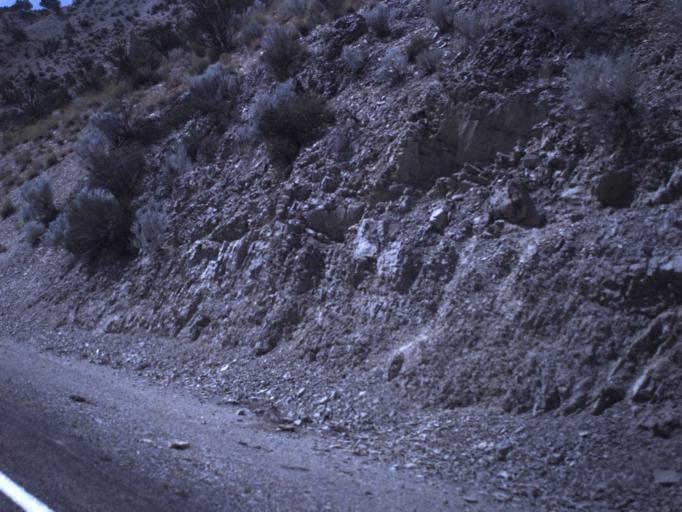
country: US
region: Utah
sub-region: Juab County
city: Nephi
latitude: 39.7133
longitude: -111.8026
